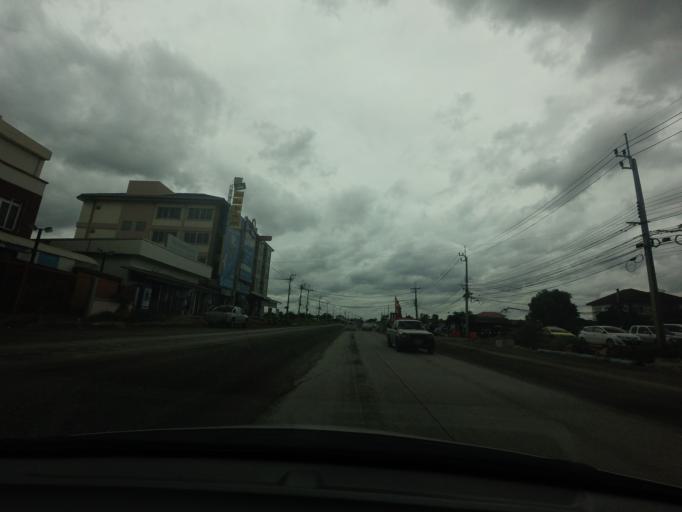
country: TH
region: Bangkok
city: Lat Krabang
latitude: 13.7670
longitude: 100.7762
